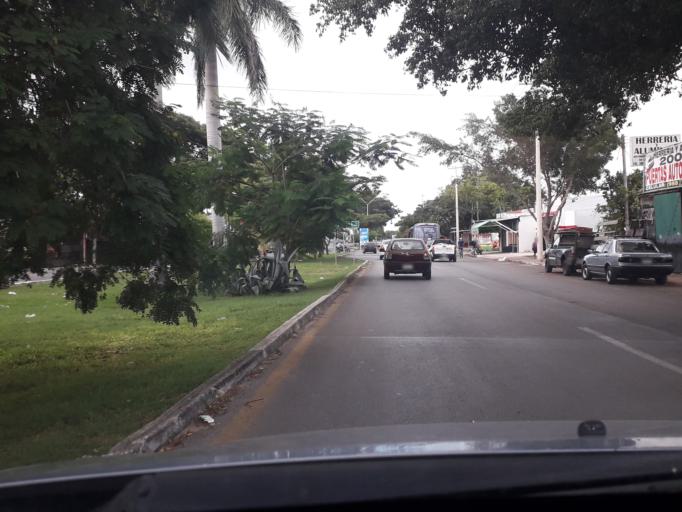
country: MX
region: Yucatan
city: Merida
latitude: 20.9636
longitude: -89.6636
